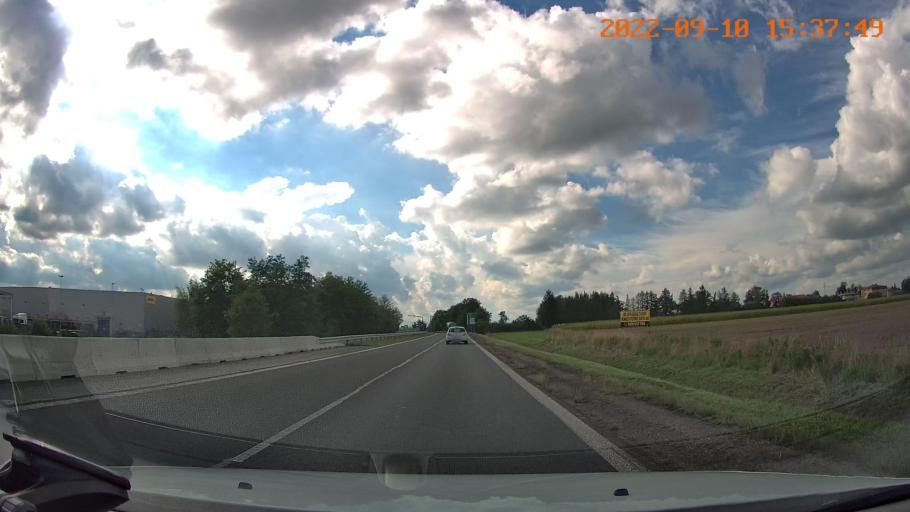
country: PL
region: Silesian Voivodeship
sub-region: Powiat bierunsko-ledzinski
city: Bierun
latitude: 50.1103
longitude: 19.0607
